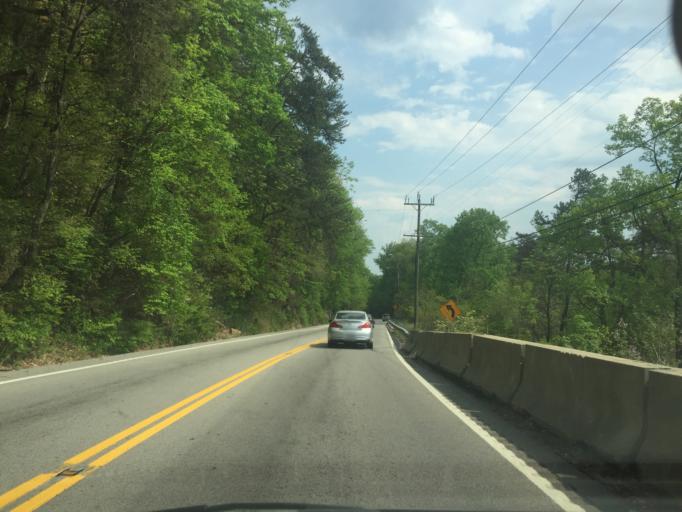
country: US
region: Tennessee
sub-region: Hamilton County
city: Signal Mountain
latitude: 35.1120
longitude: -85.3538
